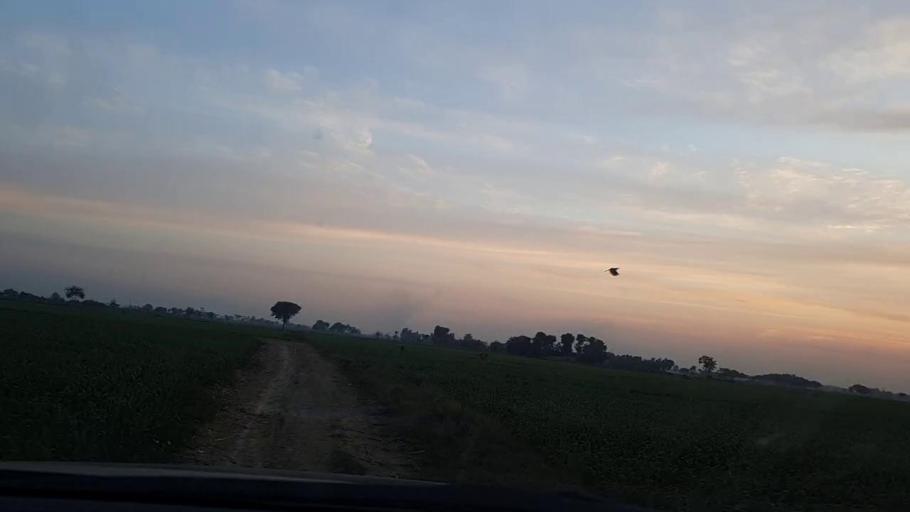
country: PK
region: Sindh
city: Sakrand
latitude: 26.1969
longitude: 68.3247
